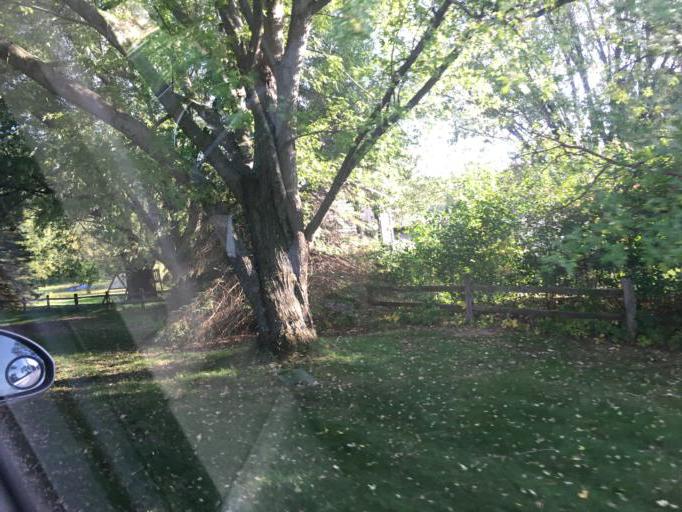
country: US
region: Minnesota
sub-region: Olmsted County
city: Rochester
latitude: 43.9936
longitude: -92.3856
